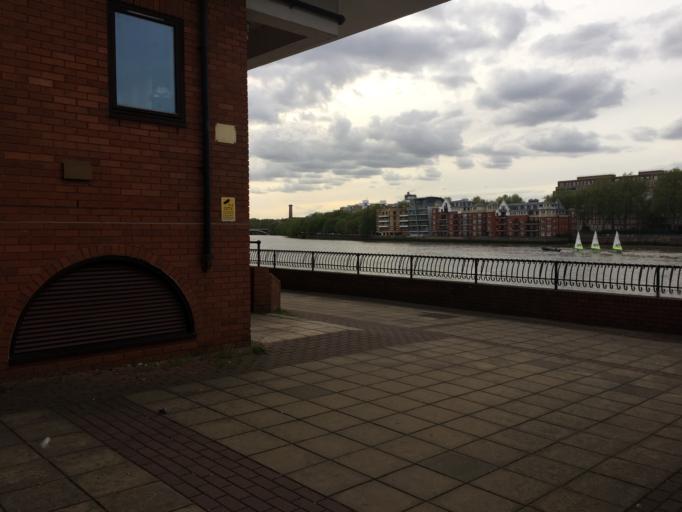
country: GB
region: England
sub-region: Greater London
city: City of Westminster
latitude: 51.4835
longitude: -0.1331
